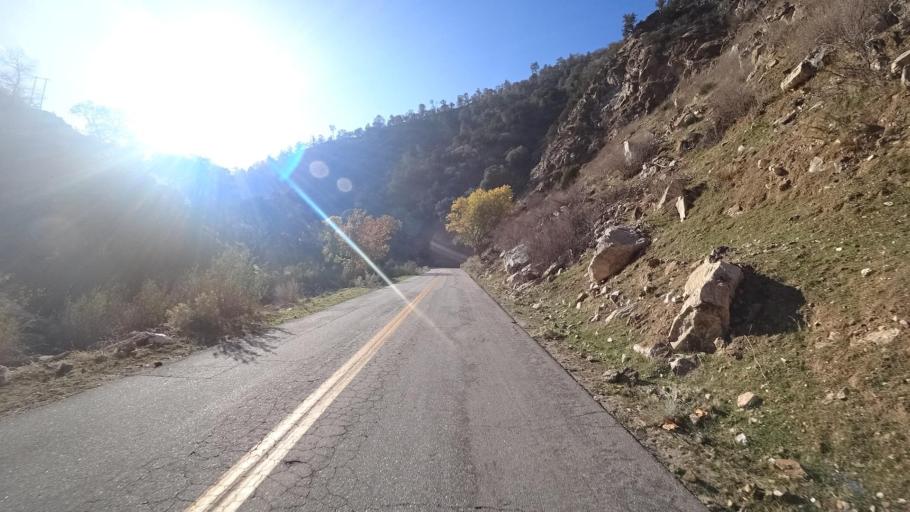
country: US
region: California
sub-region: Kern County
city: Golden Hills
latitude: 35.3099
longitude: -118.4990
